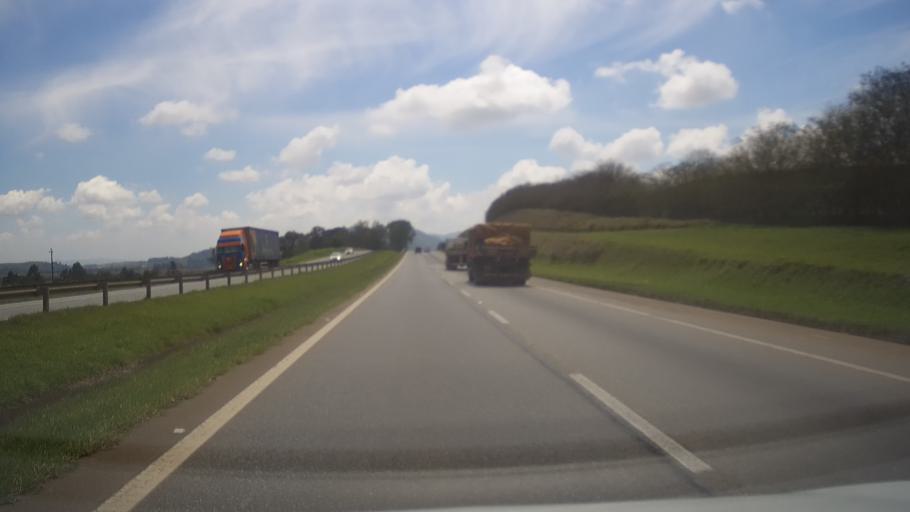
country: BR
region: Minas Gerais
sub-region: Santa Rita Do Sapucai
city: Santa Rita do Sapucai
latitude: -22.1012
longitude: -45.7222
